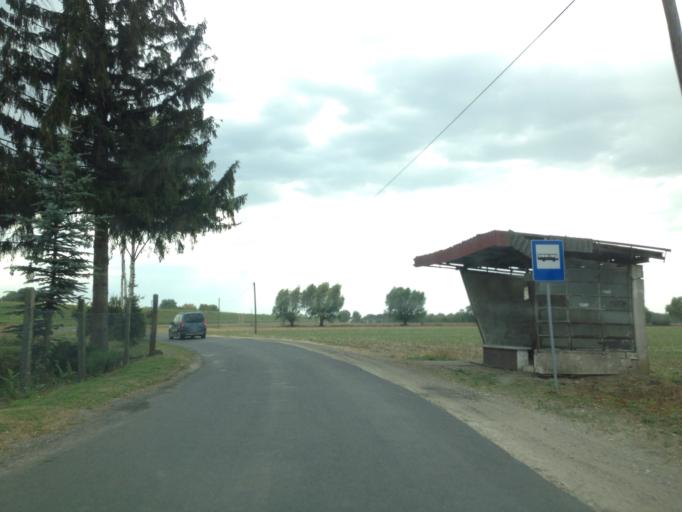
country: PL
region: Kujawsko-Pomorskie
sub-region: Powiat chelminski
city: Chelmno
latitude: 53.3554
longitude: 18.3682
